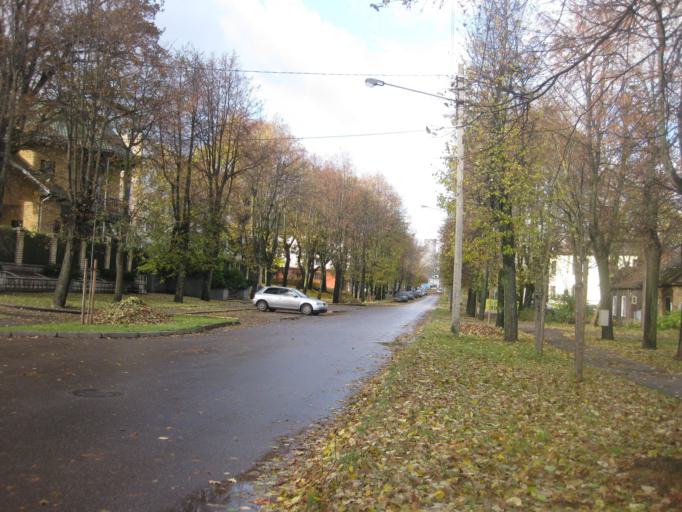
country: LT
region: Kauno apskritis
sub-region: Kaunas
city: Eiguliai
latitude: 54.9042
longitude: 23.9357
